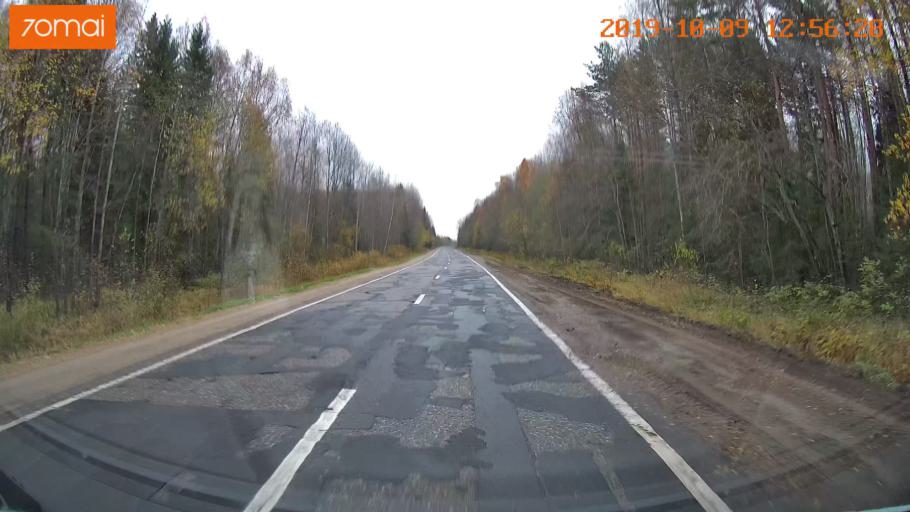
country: RU
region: Jaroslavl
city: Prechistoye
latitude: 58.3947
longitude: 40.4166
